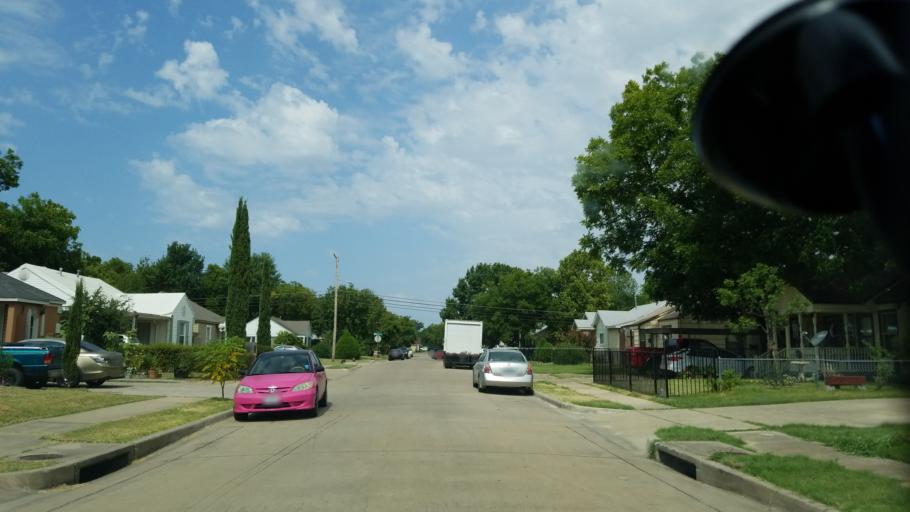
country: US
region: Texas
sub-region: Dallas County
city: Grand Prairie
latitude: 32.7504
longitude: -96.9834
